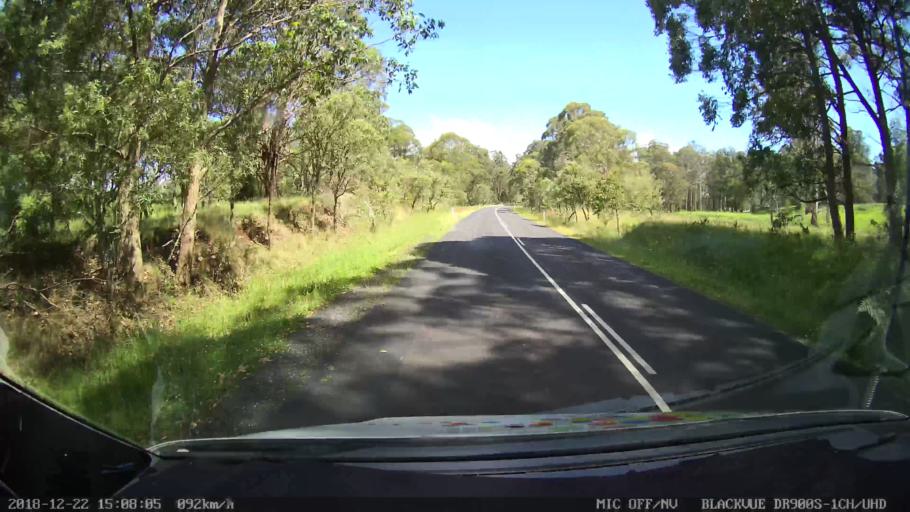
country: AU
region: New South Wales
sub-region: Bellingen
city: Dorrigo
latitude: -30.3076
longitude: 152.4136
